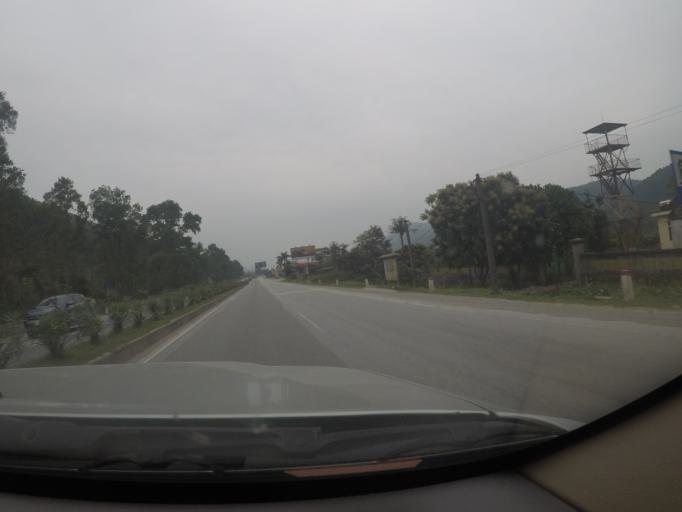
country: VN
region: Nghe An
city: Dien Chau
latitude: 18.8786
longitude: 105.6115
